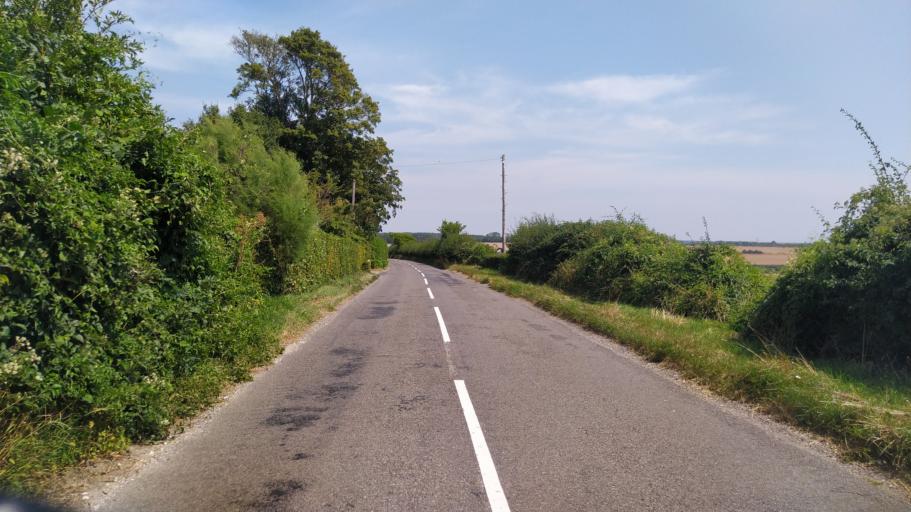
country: GB
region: England
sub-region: Hampshire
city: Cowplain
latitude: 50.9479
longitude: -1.0006
